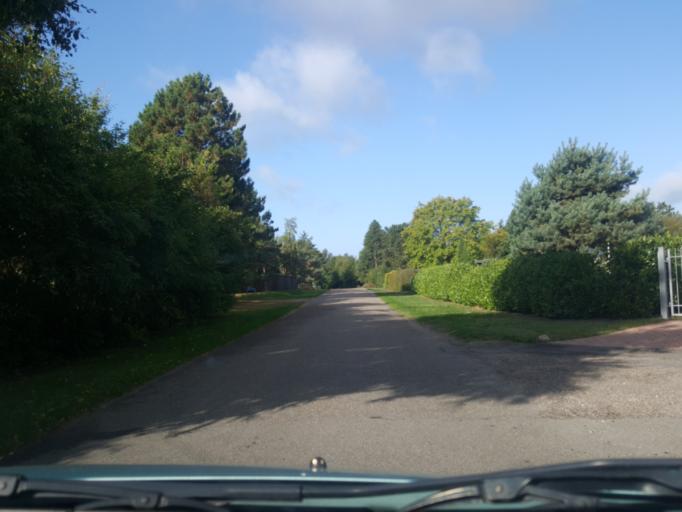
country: DK
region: Zealand
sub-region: Guldborgsund Kommune
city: Nykobing Falster
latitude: 54.6538
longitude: 11.9530
